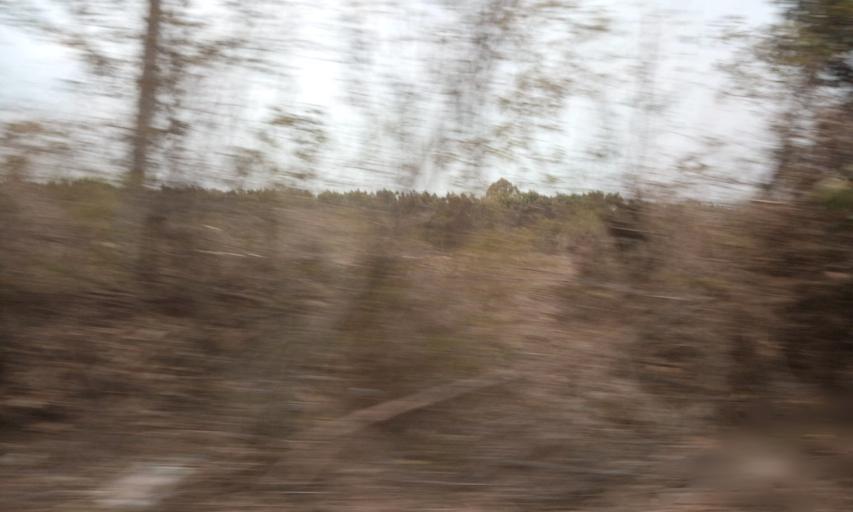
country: TH
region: Phayao
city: Phu Sang
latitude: 19.5830
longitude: 100.3086
